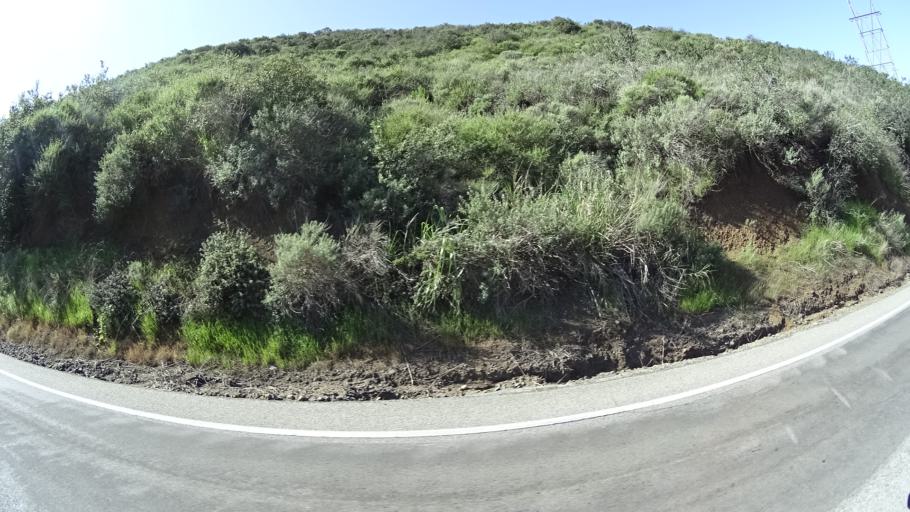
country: US
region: California
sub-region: Ventura County
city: Casa Conejo
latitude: 34.1592
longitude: -118.9967
